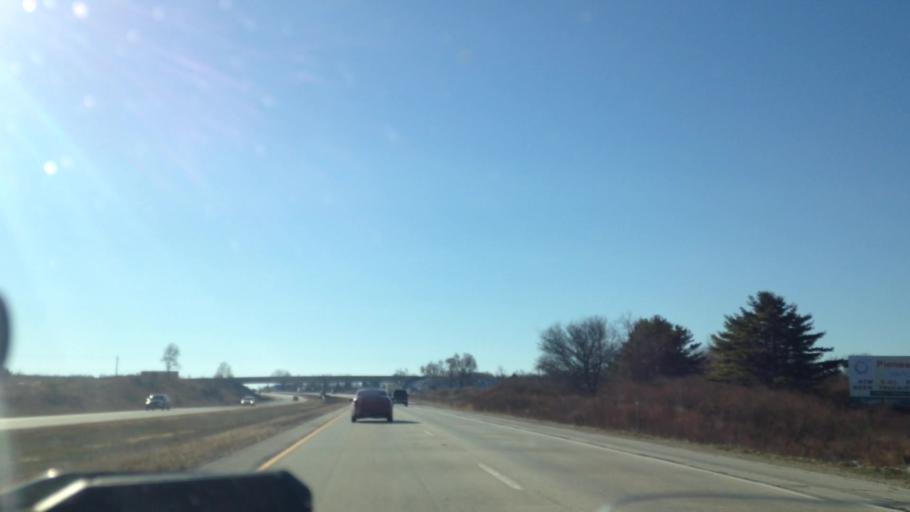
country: US
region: Wisconsin
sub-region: Washington County
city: Jackson
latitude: 43.2986
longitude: -88.1871
